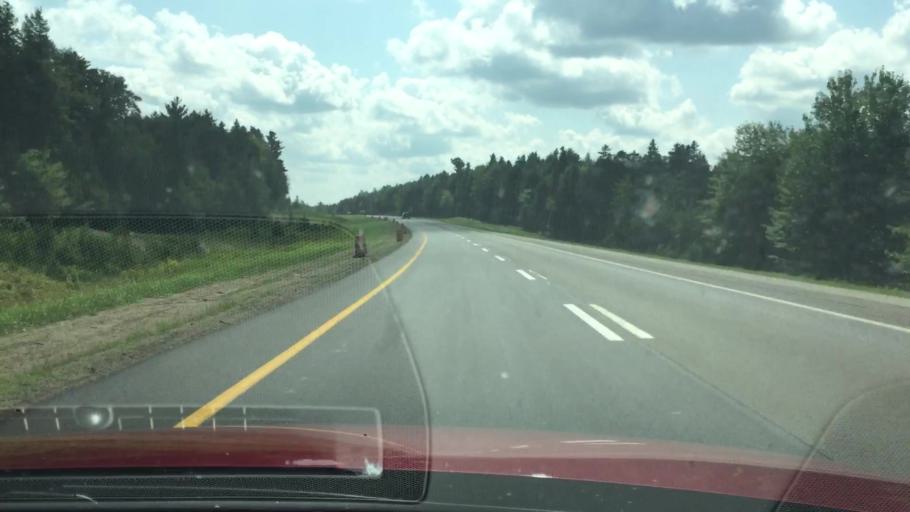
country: US
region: Maine
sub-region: Penobscot County
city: Medway
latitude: 45.6731
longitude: -68.4989
